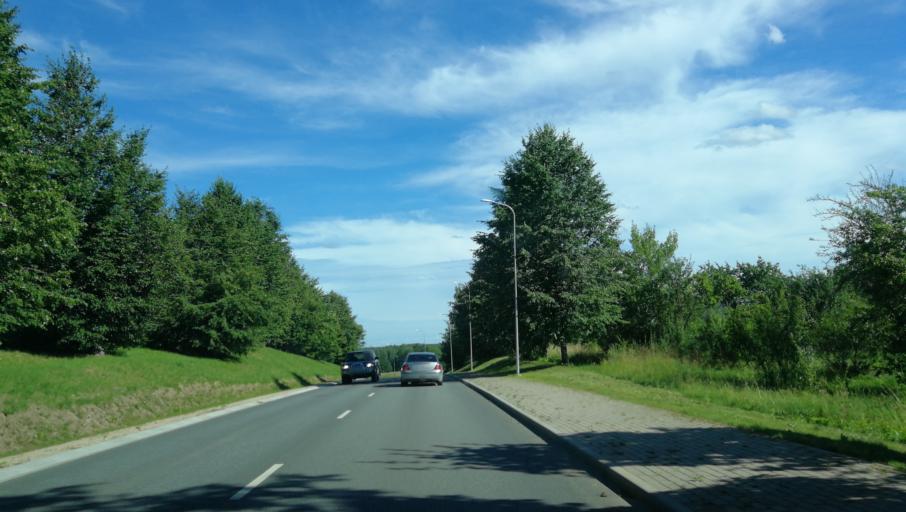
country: LV
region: Cesvaine
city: Cesvaine
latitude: 56.9656
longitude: 26.3197
